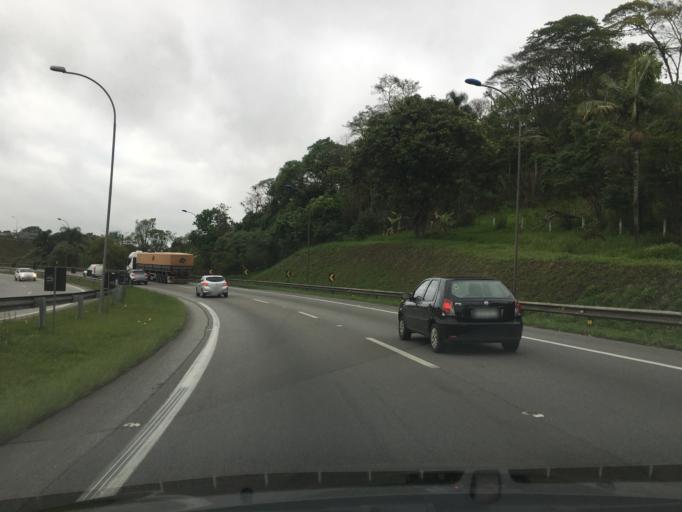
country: BR
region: Sao Paulo
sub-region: Embu
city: Embu
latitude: -23.6298
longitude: -46.8324
